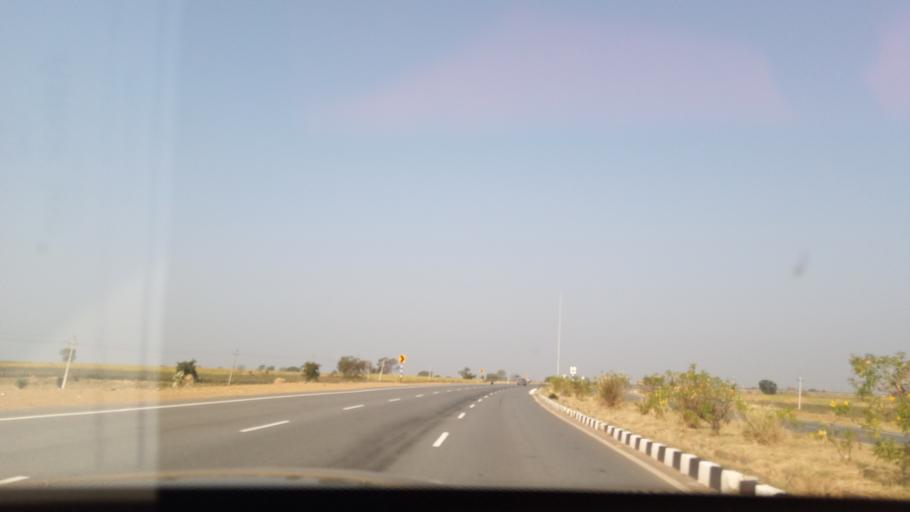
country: IN
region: Karnataka
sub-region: Haveri
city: Haveri
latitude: 14.8418
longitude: 75.3426
